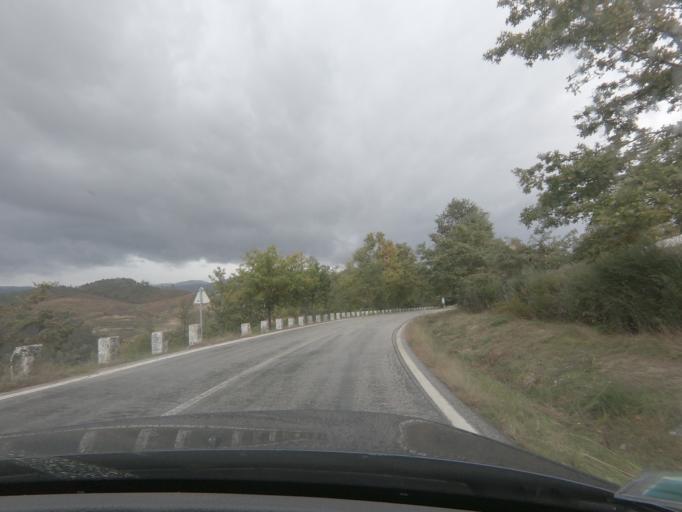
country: PT
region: Vila Real
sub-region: Mondim de Basto
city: Mondim de Basto
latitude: 41.3977
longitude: -7.9611
